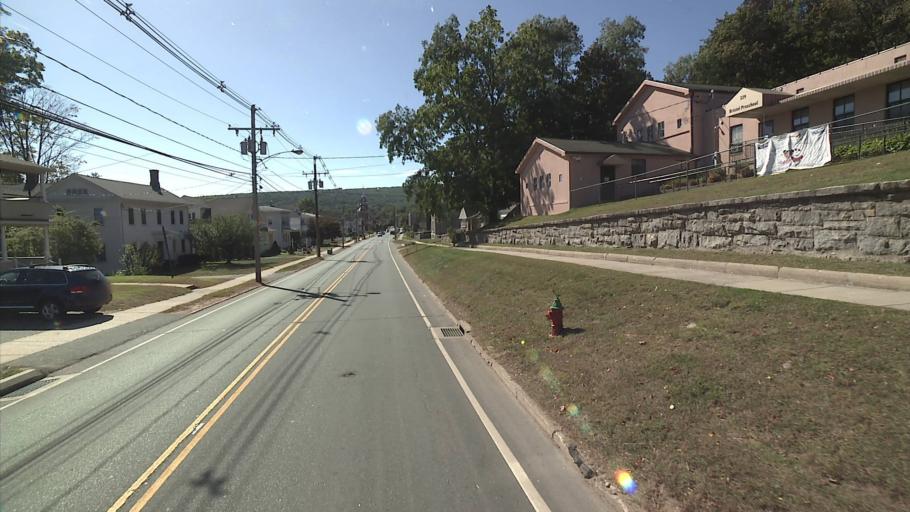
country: US
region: Connecticut
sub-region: Hartford County
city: Bristol
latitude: 41.6768
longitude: -72.9507
